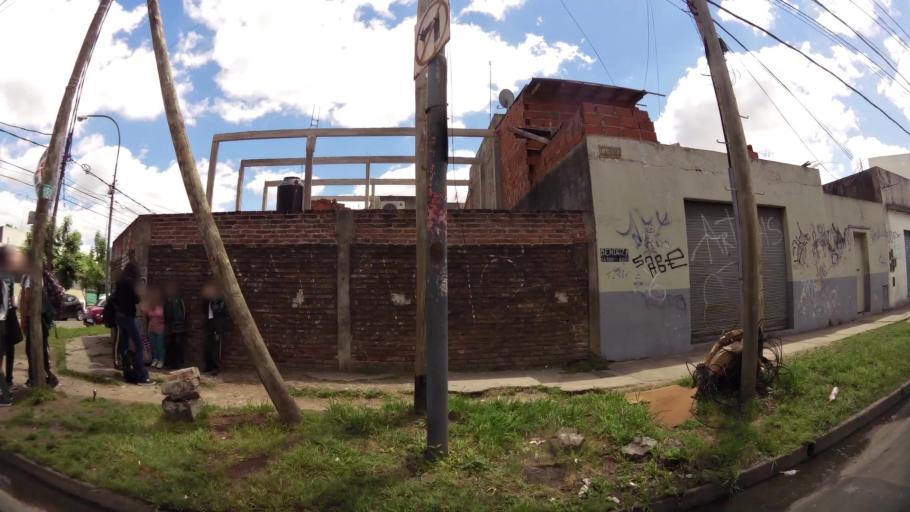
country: AR
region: Buenos Aires
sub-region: Partido de Lanus
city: Lanus
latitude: -34.7030
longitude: -58.4292
